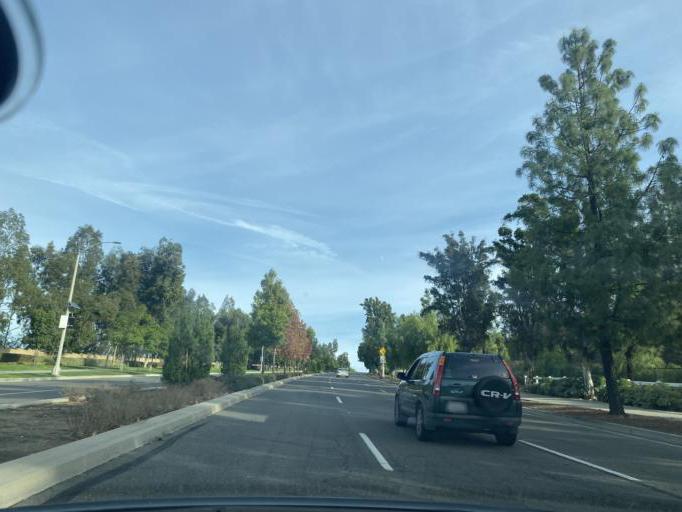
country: US
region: California
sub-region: Orange County
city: Brea
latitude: 33.8993
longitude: -117.8975
